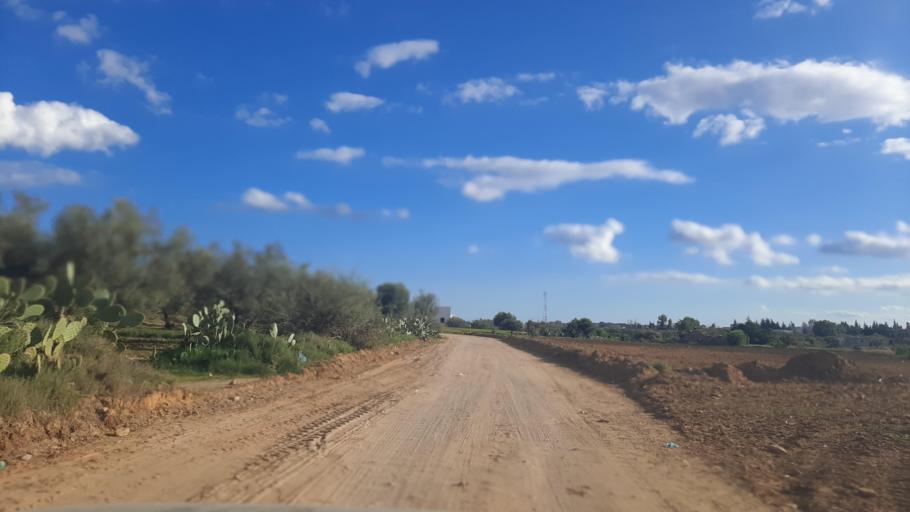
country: TN
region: Nabul
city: Al Hammamat
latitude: 36.4227
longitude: 10.5086
